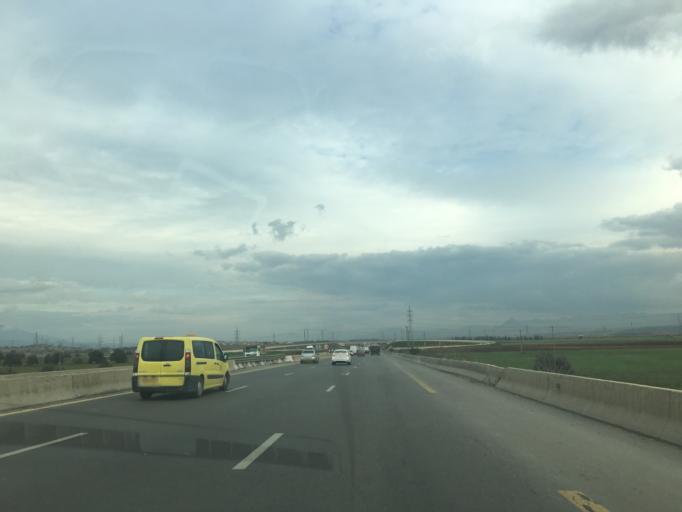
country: DZ
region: Bouira
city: Bouira
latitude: 36.3312
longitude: 3.9368
